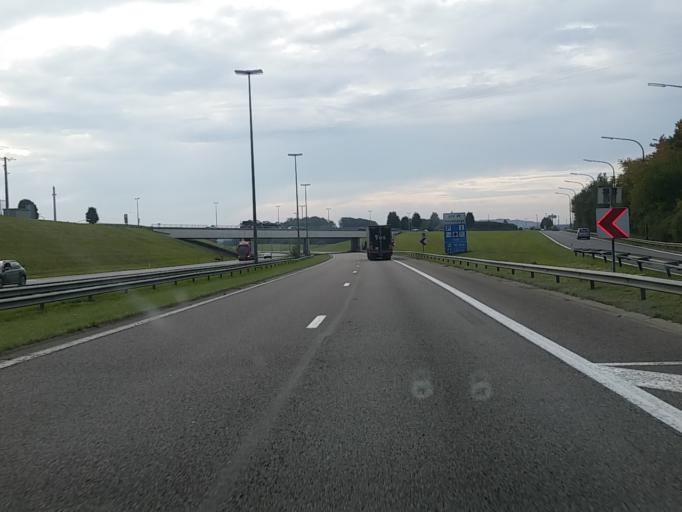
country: BE
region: Wallonia
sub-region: Province du Luxembourg
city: Arlon
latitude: 49.6534
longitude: 5.8174
